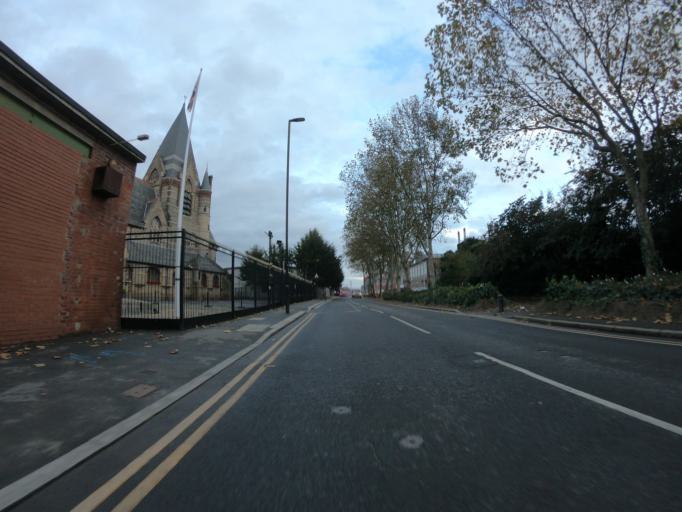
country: GB
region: England
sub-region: Greater London
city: Woolwich
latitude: 51.5025
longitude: 0.0424
